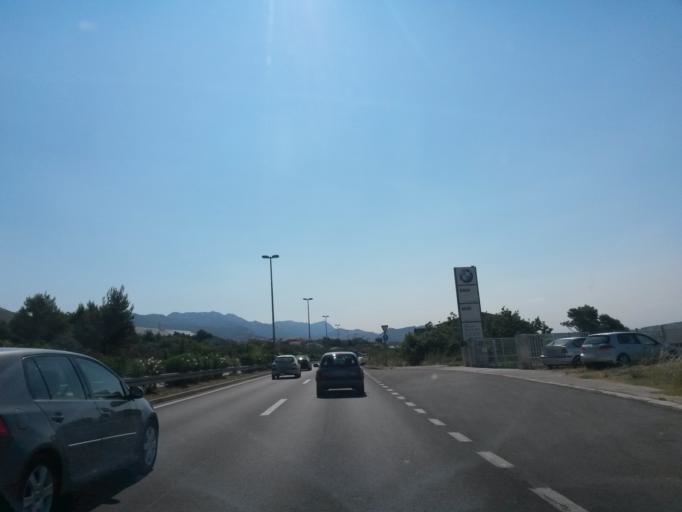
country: HR
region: Splitsko-Dalmatinska
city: Vranjic
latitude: 43.5499
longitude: 16.4368
